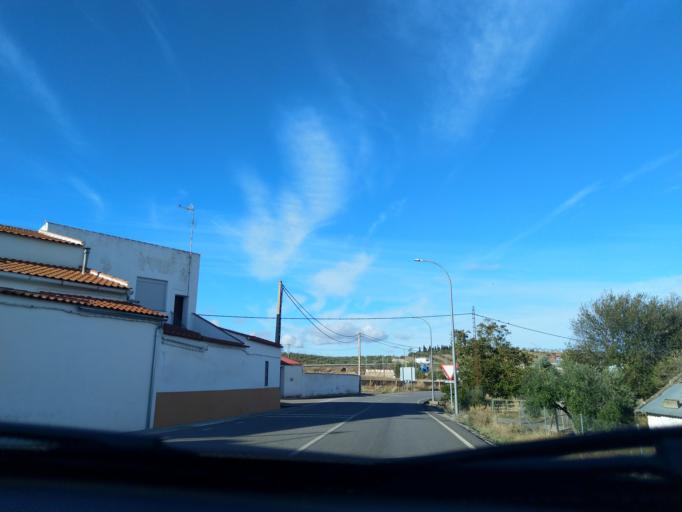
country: ES
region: Extremadura
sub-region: Provincia de Badajoz
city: Ahillones
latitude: 38.2621
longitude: -5.8620
